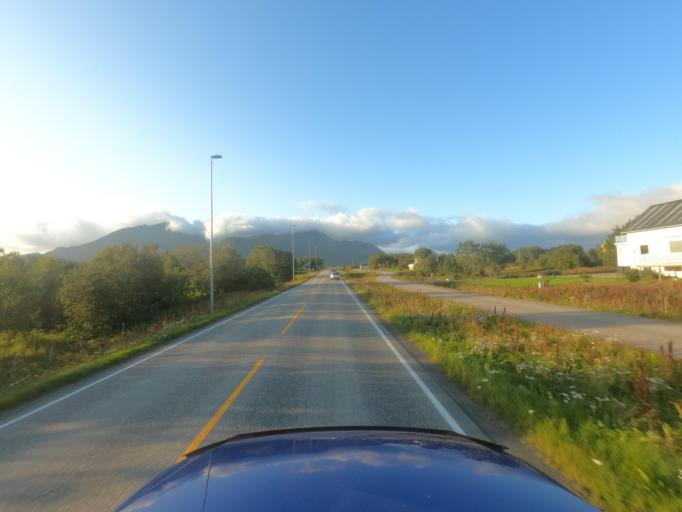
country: NO
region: Nordland
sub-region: Vestvagoy
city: Leknes
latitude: 68.1714
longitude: 13.6316
